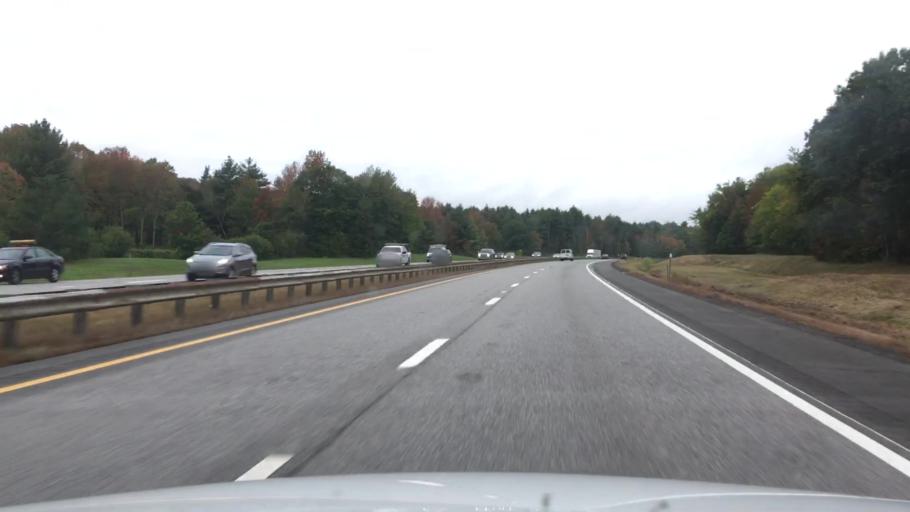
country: US
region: Maine
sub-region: Cumberland County
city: Cumberland Center
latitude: 43.7615
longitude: -70.3095
